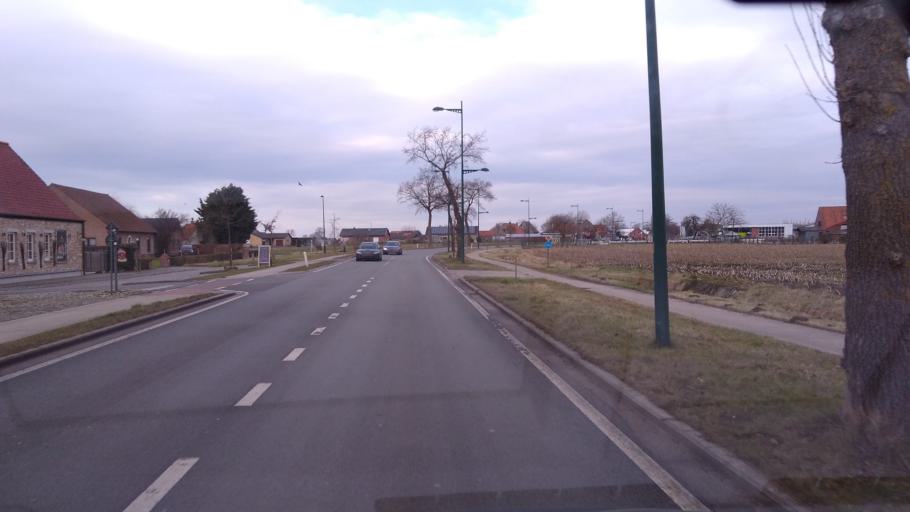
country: BE
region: Flanders
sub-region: Provincie Oost-Vlaanderen
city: Aalter
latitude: 51.0570
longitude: 3.4584
